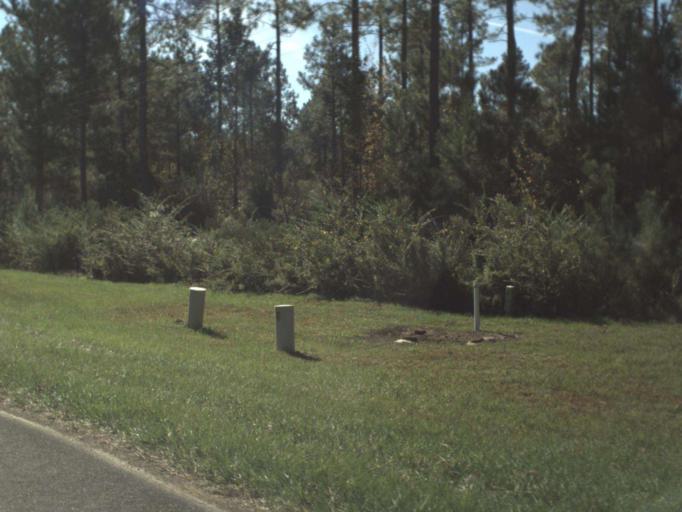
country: US
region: Florida
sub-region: Okaloosa County
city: Crestview
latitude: 30.9347
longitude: -86.6354
